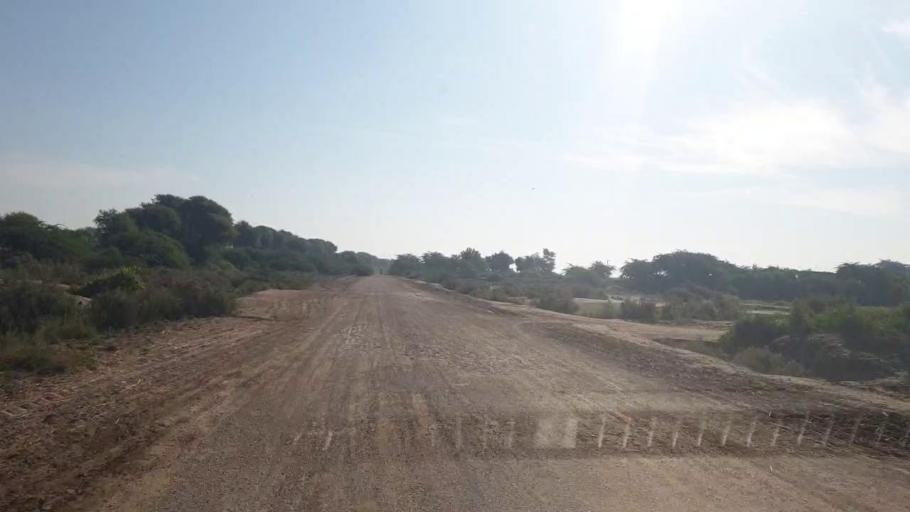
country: PK
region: Sindh
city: Rajo Khanani
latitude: 24.9712
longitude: 68.7903
